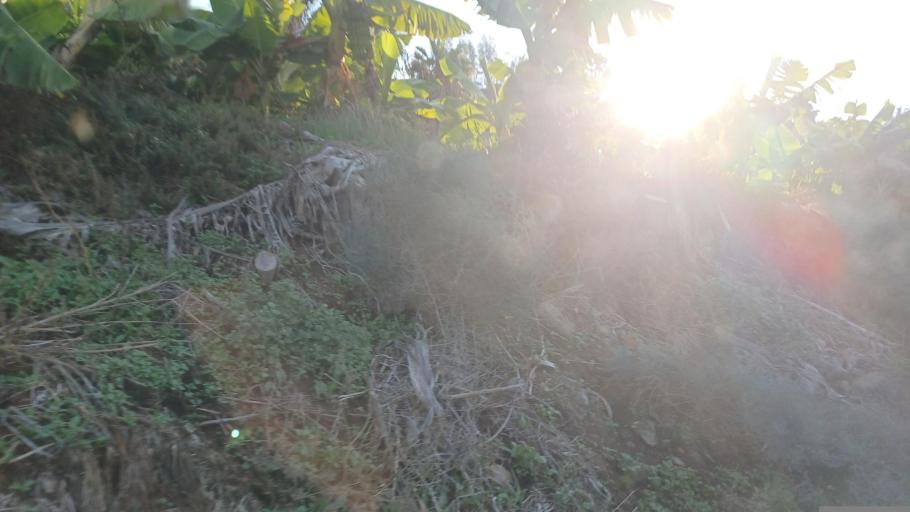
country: CY
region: Pafos
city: Kissonerga
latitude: 34.8343
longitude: 32.3954
